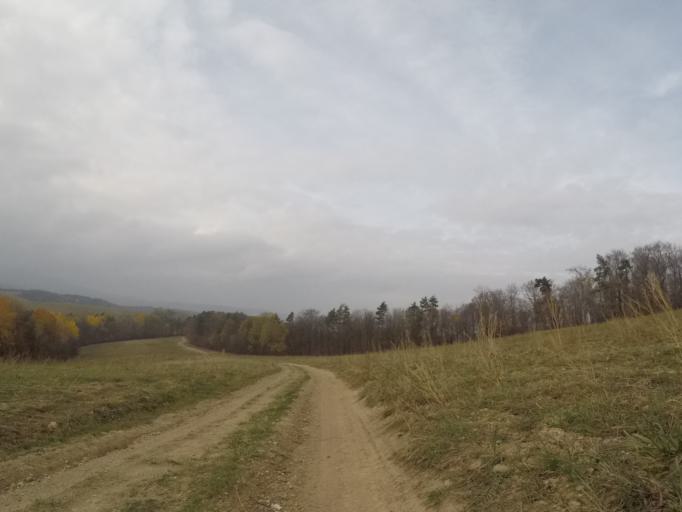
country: SK
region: Presovsky
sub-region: Okres Presov
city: Presov
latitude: 48.9350
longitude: 21.1277
